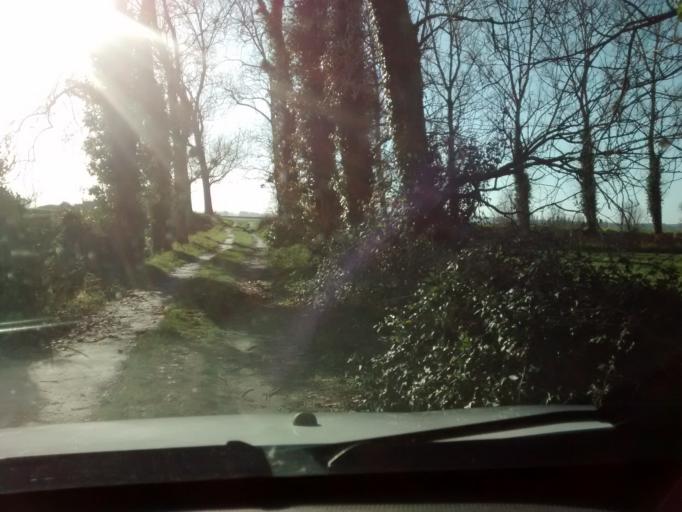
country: FR
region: Brittany
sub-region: Departement d'Ille-et-Vilaine
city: Roz-sur-Couesnon
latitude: 48.6276
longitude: -1.5344
